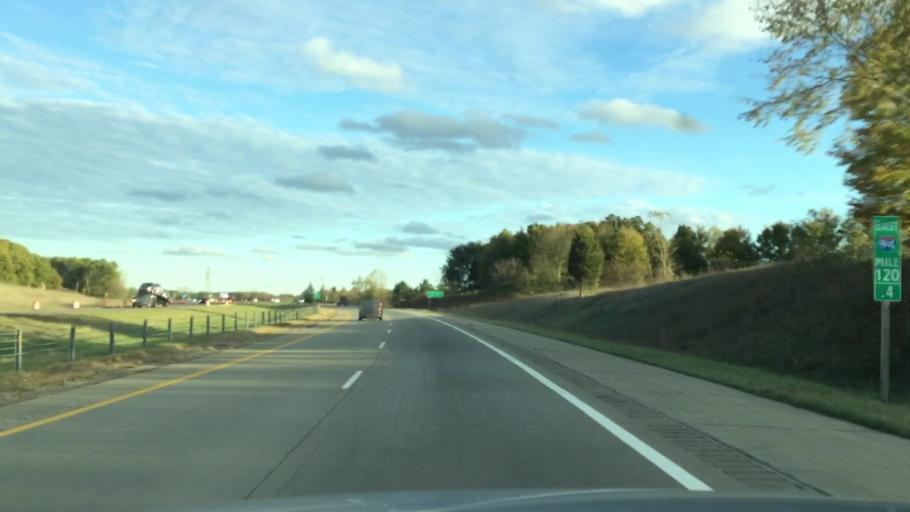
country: US
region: Michigan
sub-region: Calhoun County
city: Albion
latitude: 42.2671
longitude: -84.7754
